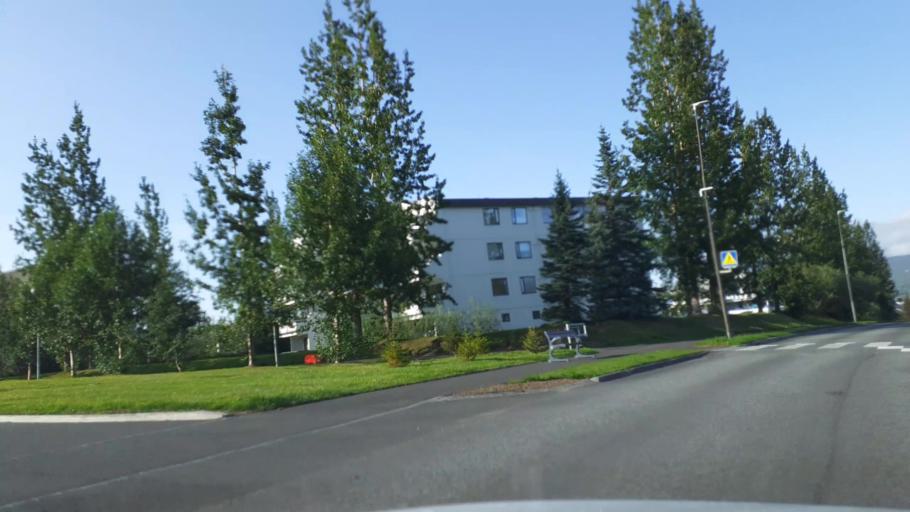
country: IS
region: Northeast
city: Akureyri
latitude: 65.6925
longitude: -18.1350
